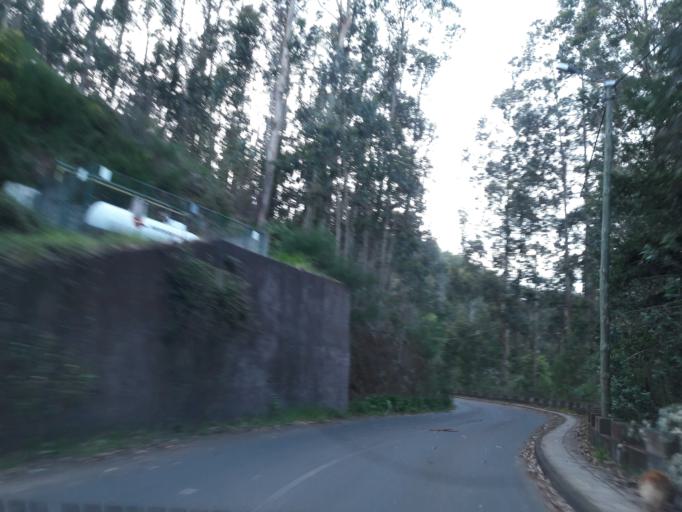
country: PT
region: Madeira
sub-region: Santa Cruz
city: Camacha
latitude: 32.6889
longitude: -16.8648
